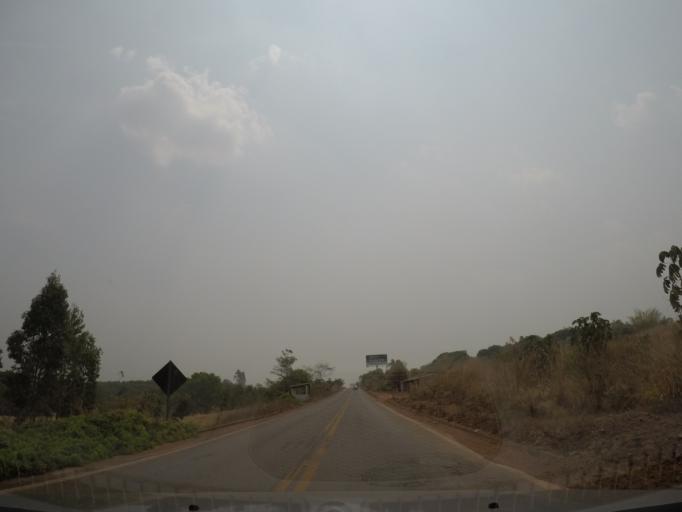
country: BR
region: Goias
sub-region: Pirenopolis
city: Pirenopolis
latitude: -15.9013
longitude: -48.8678
